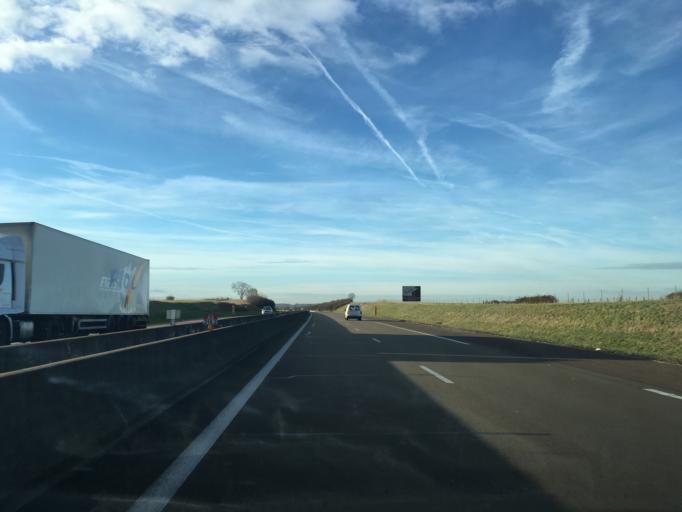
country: FR
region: Bourgogne
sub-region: Departement de l'Yonne
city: Avallon
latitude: 47.5013
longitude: 4.1052
